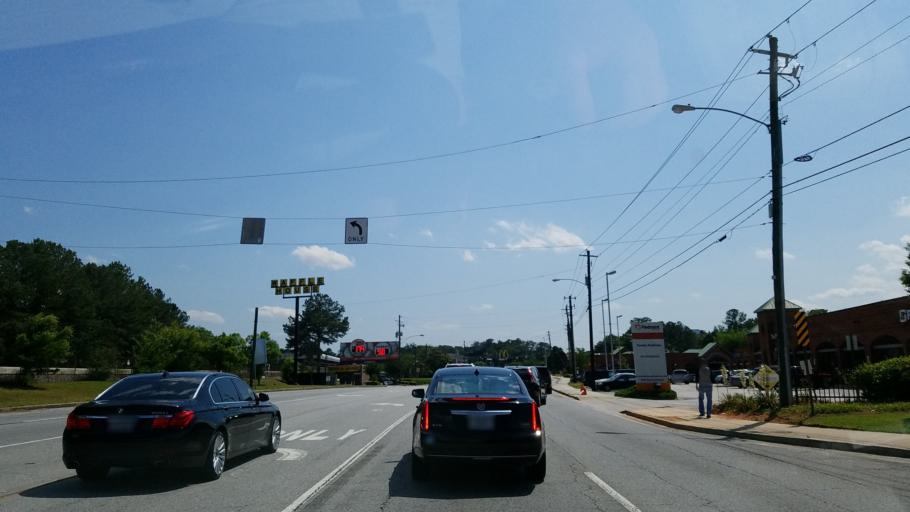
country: US
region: Georgia
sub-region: DeKalb County
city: North Atlanta
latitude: 33.8625
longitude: -84.3385
